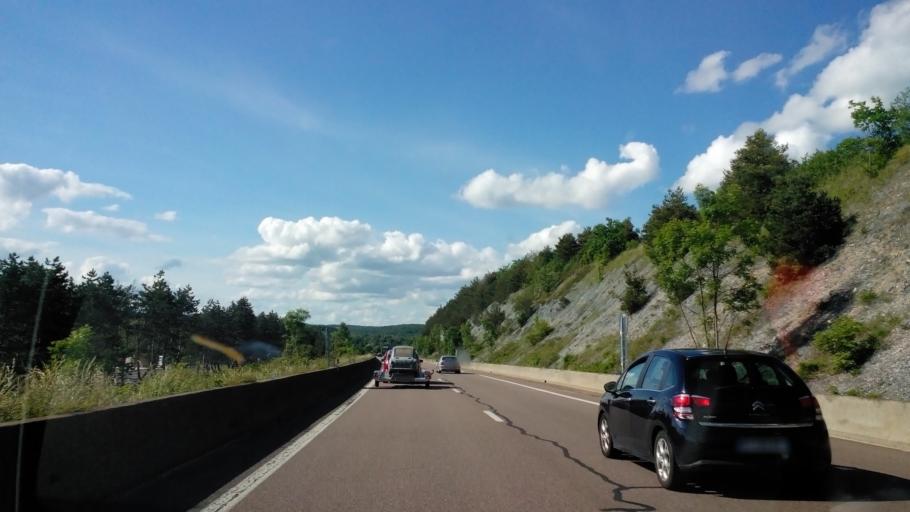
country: FR
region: Bourgogne
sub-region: Departement de la Cote-d'Or
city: Savigny-les-Beaune
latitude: 47.1539
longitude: 4.6991
